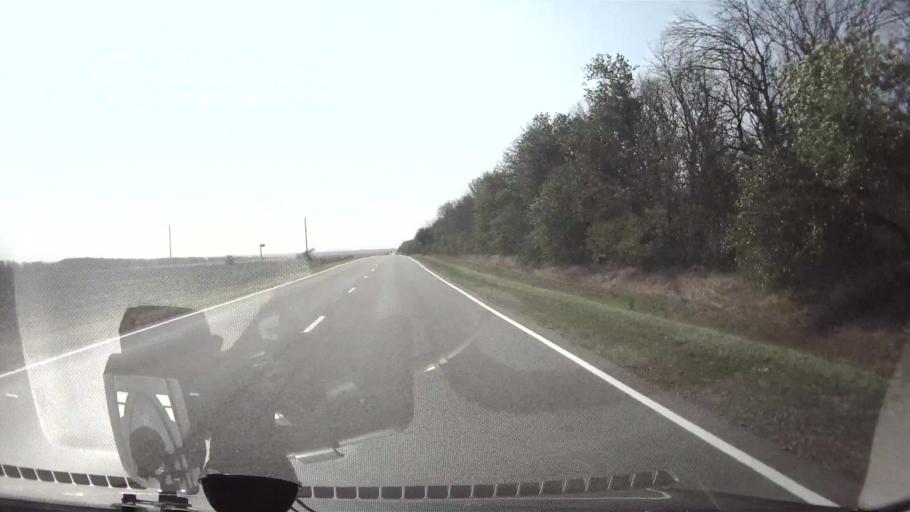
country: RU
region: Krasnodarskiy
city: Dmitriyevskaya
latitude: 45.7835
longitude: 40.7191
